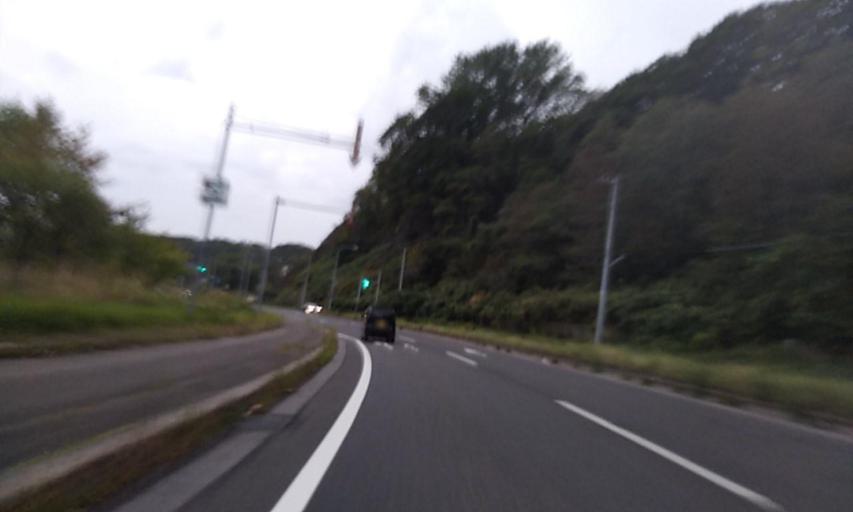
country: JP
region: Hokkaido
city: Abashiri
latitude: 44.0151
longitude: 144.2809
